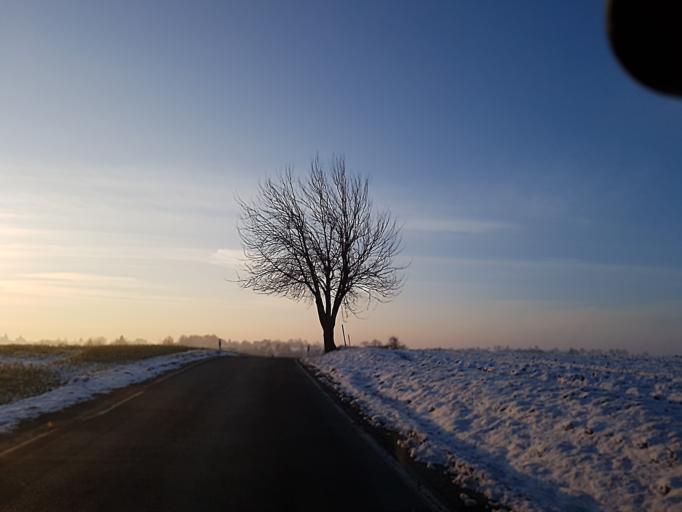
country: DE
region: Saxony
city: Grossweitzschen
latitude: 51.1833
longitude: 13.0359
